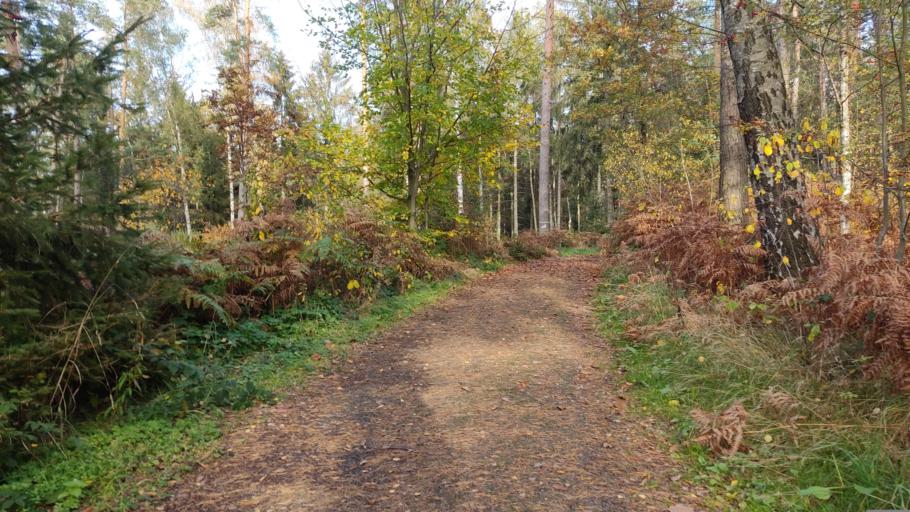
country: DE
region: Saxony
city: Struppen
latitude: 50.8981
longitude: 14.0329
